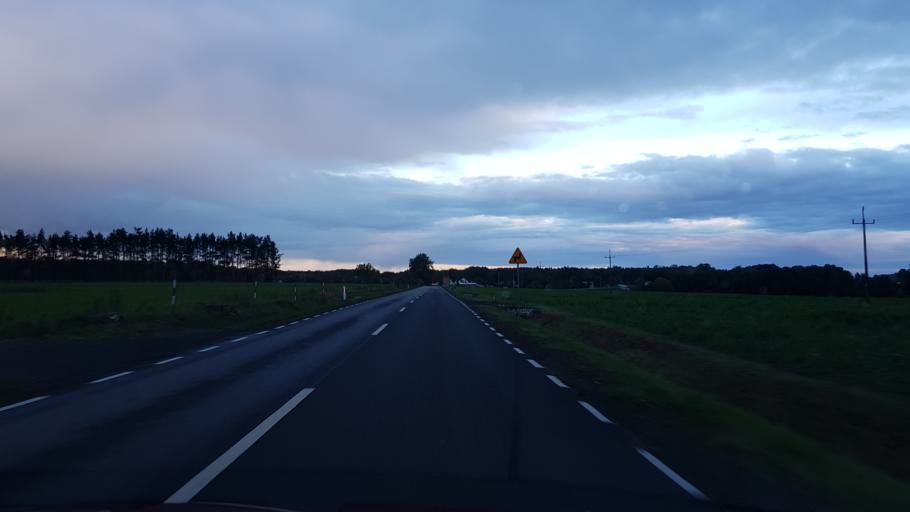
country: PL
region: Greater Poland Voivodeship
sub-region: Powiat zlotowski
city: Krajenka
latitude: 53.2729
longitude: 16.9398
